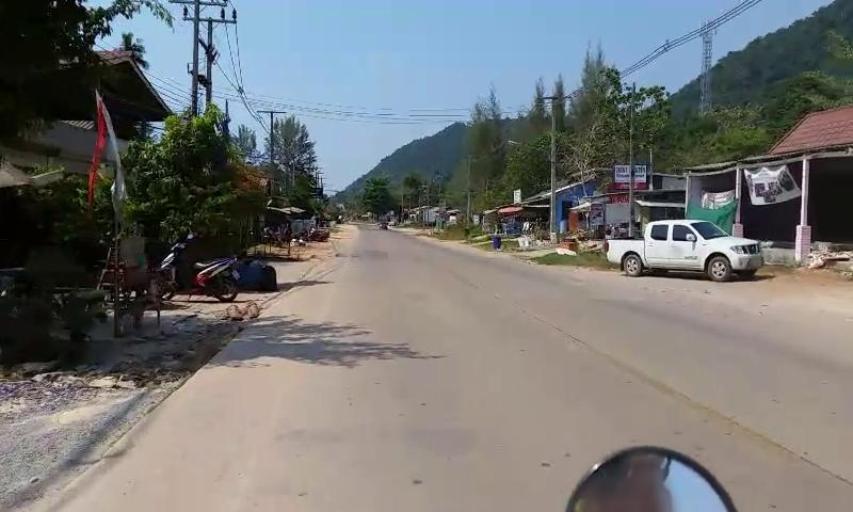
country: TH
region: Krabi
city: Saladan
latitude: 7.6243
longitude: 99.0331
